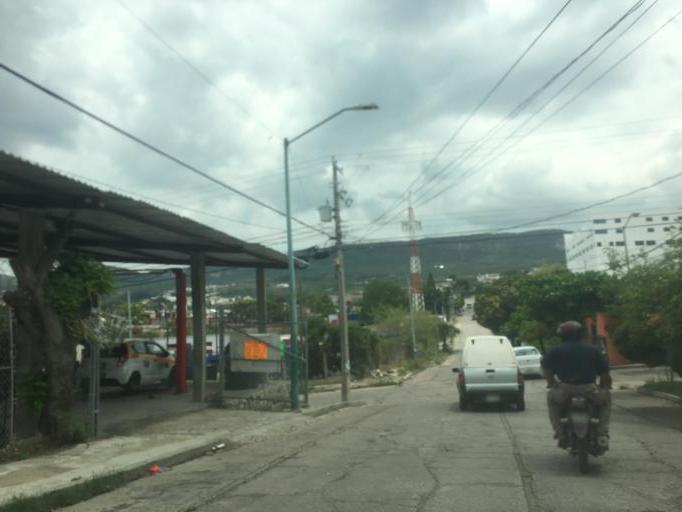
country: MX
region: Chiapas
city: Tuxtla Gutierrez
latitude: 16.7459
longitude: -93.1256
